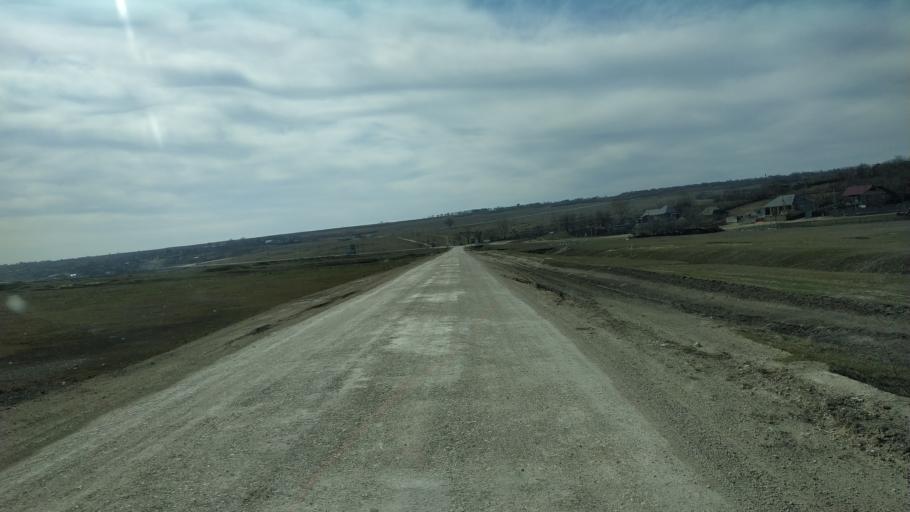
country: MD
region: Nisporeni
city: Nisporeni
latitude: 46.9728
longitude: 28.1848
